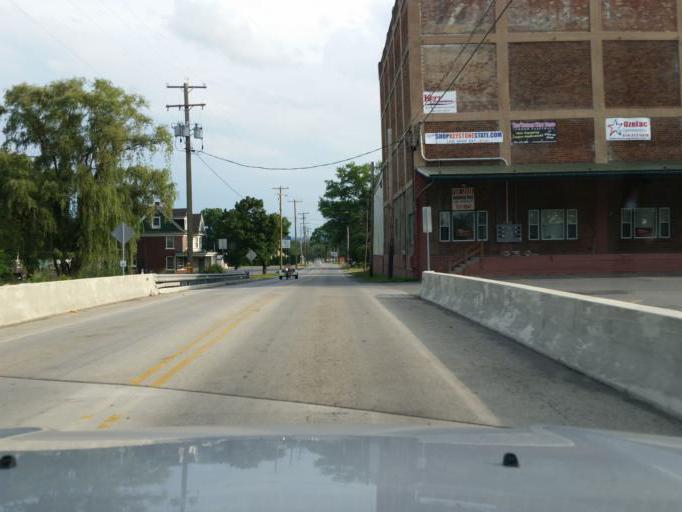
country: US
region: Pennsylvania
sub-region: Blair County
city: Lakemont
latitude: 40.4633
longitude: -78.4271
